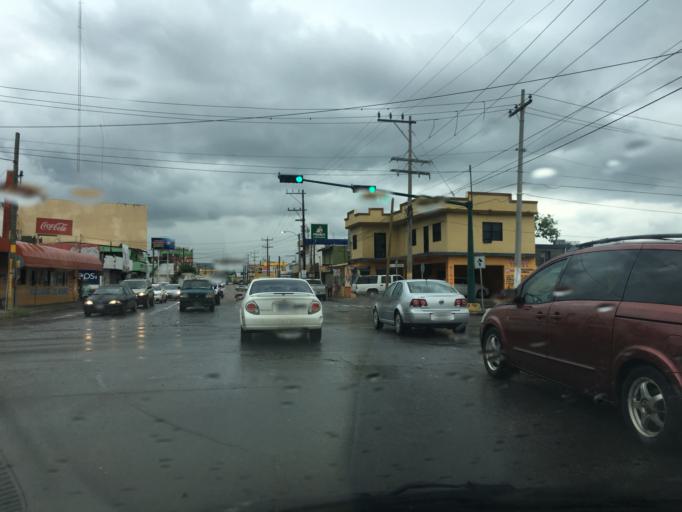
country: MX
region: Tamaulipas
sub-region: Matamoros
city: Heroica Matamoros
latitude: 25.8764
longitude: -97.5182
